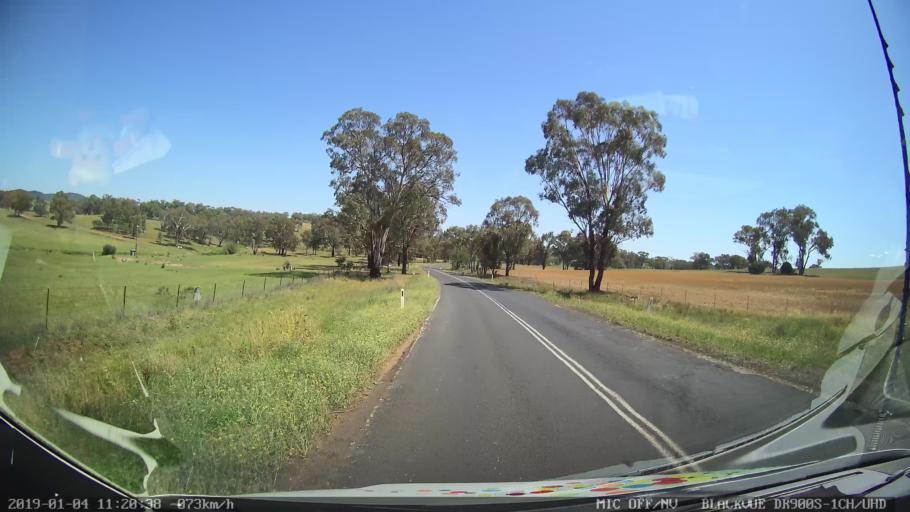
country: AU
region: New South Wales
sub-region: Cabonne
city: Molong
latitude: -33.1618
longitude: 148.7065
